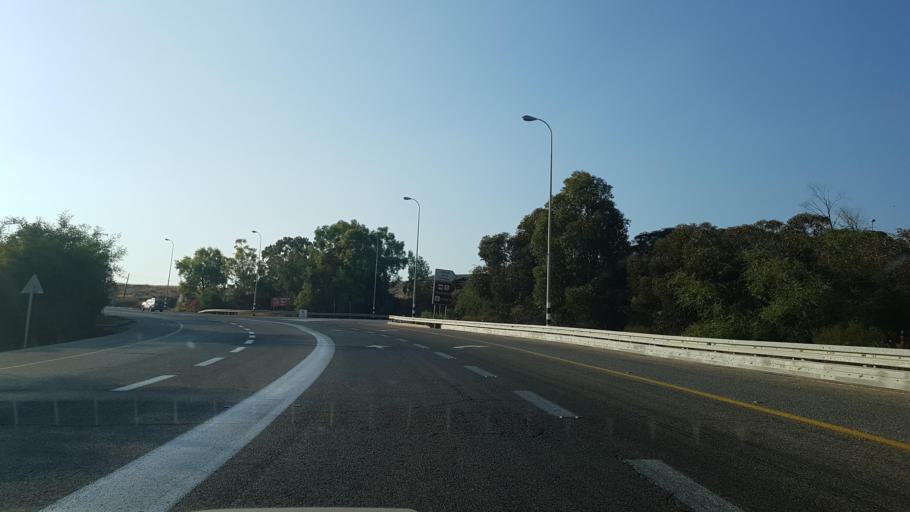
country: SY
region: Quneitra
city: Al Butayhah
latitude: 32.9122
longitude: 35.5977
